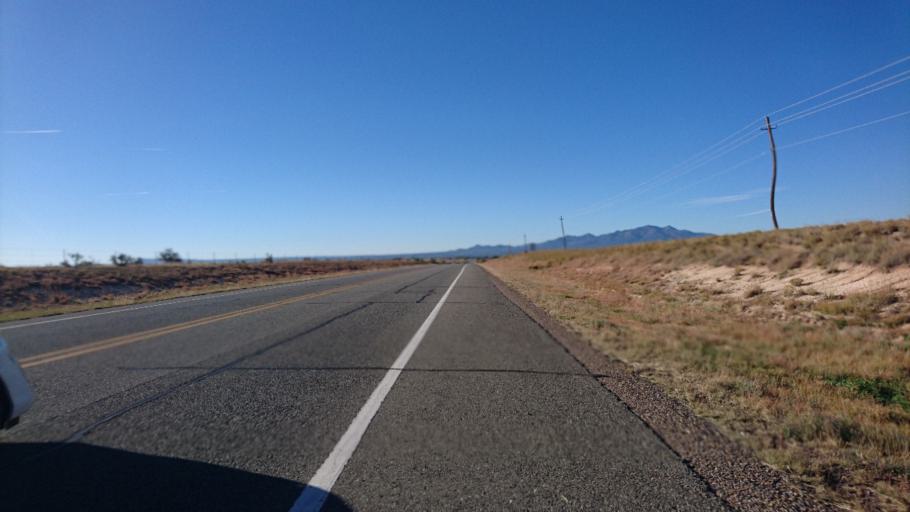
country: US
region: New Mexico
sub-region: Santa Fe County
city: La Cienega
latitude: 35.5075
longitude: -106.0626
